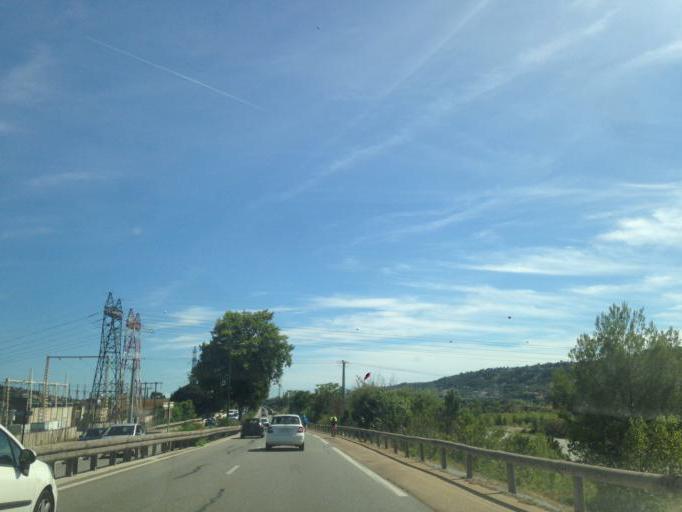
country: FR
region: Provence-Alpes-Cote d'Azur
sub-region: Departement des Alpes-Maritimes
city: La Gaude
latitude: 43.7208
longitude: 7.1862
